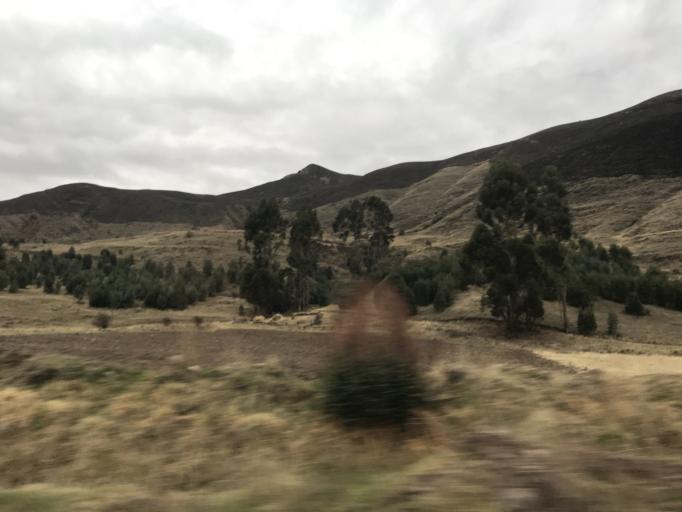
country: PE
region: Cusco
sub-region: Provincia de Anta
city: Huarocondo
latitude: -13.4431
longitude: -72.2056
